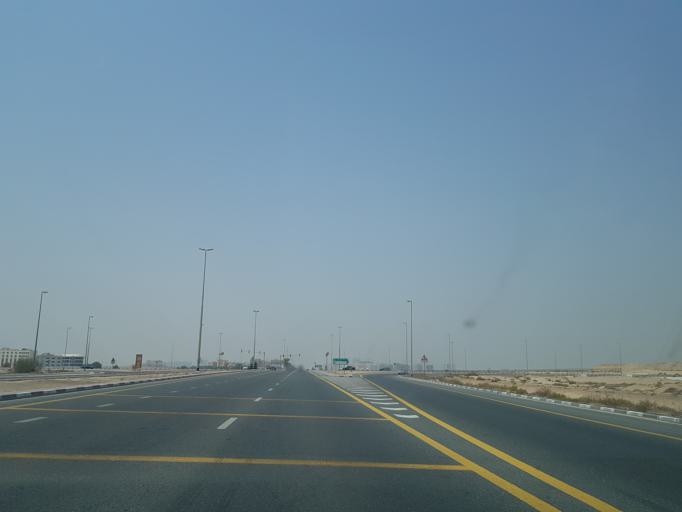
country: AE
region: Ash Shariqah
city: Sharjah
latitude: 25.1402
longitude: 55.4286
